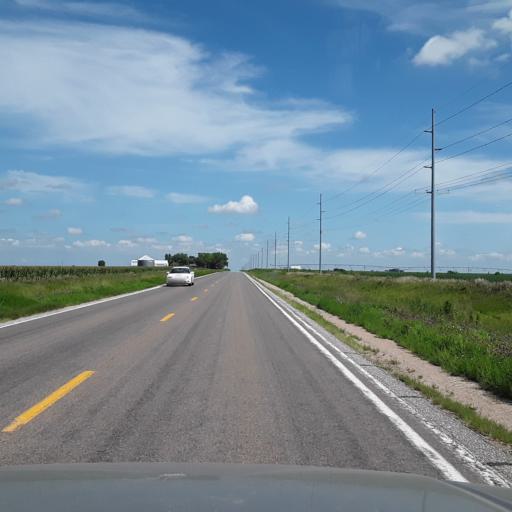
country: US
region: Nebraska
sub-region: York County
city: York
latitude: 40.9382
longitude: -97.4062
